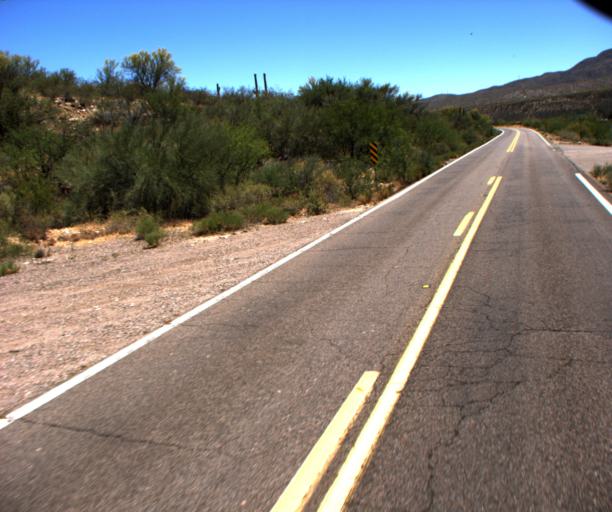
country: US
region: Arizona
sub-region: Pinal County
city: Kearny
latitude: 33.1156
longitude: -110.7707
